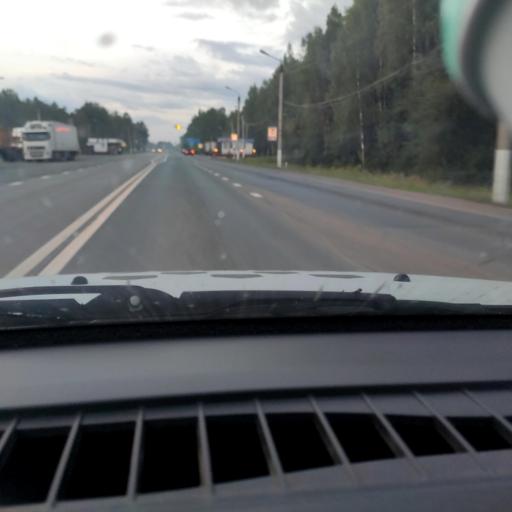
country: RU
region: Kirov
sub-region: Kirovo-Chepetskiy Rayon
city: Kirov
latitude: 58.6807
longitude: 49.6447
